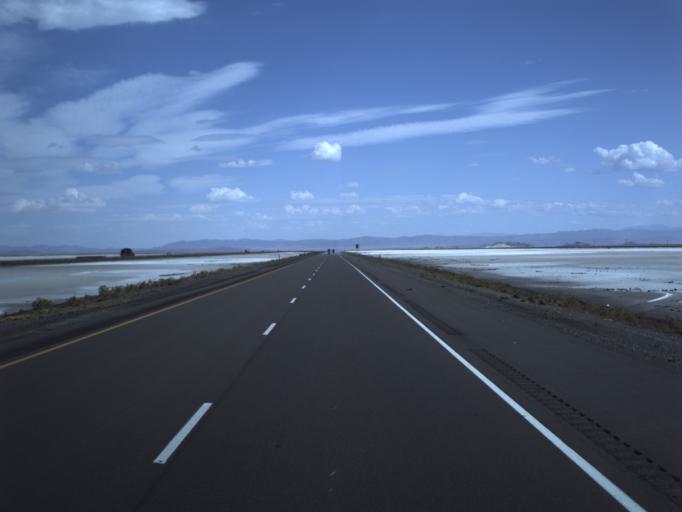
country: US
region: Utah
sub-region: Tooele County
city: Wendover
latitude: 40.7293
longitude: -113.4300
